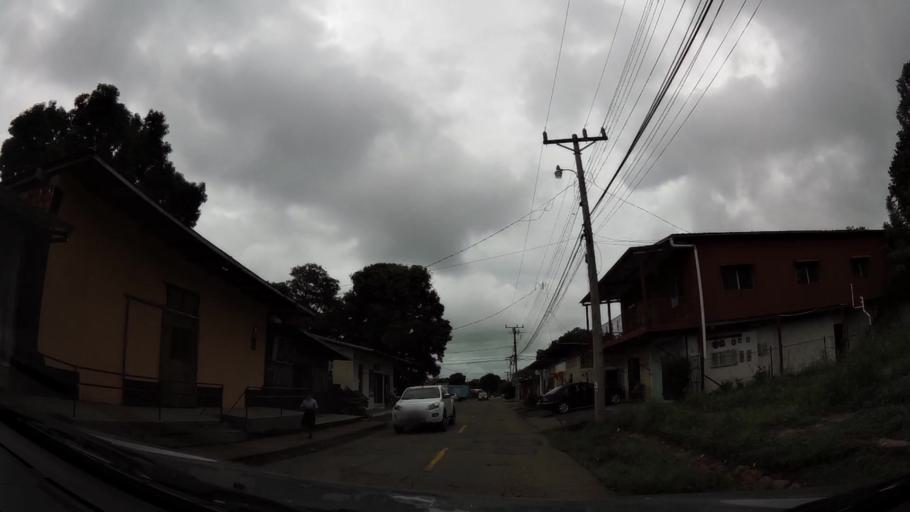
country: PA
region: Chiriqui
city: Dolega District
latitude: 8.5627
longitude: -82.4142
